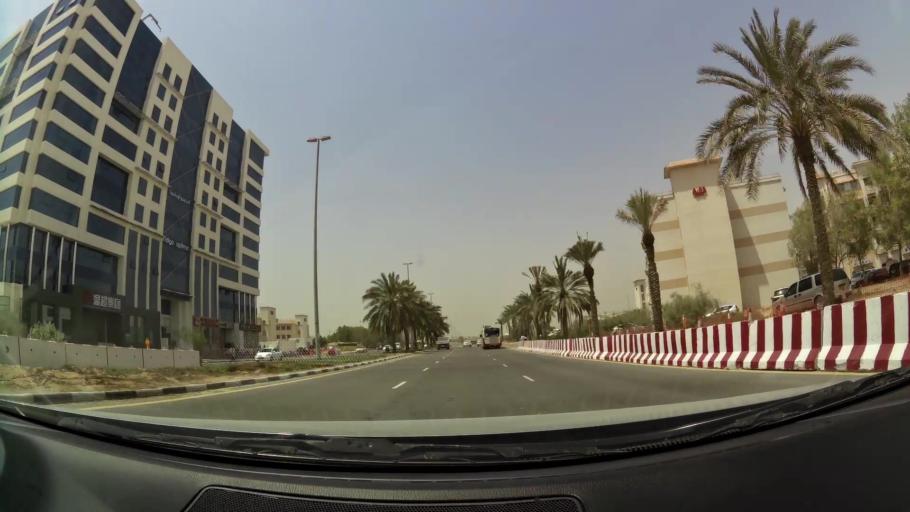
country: AE
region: Ash Shariqah
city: Sharjah
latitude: 25.1702
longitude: 55.4094
